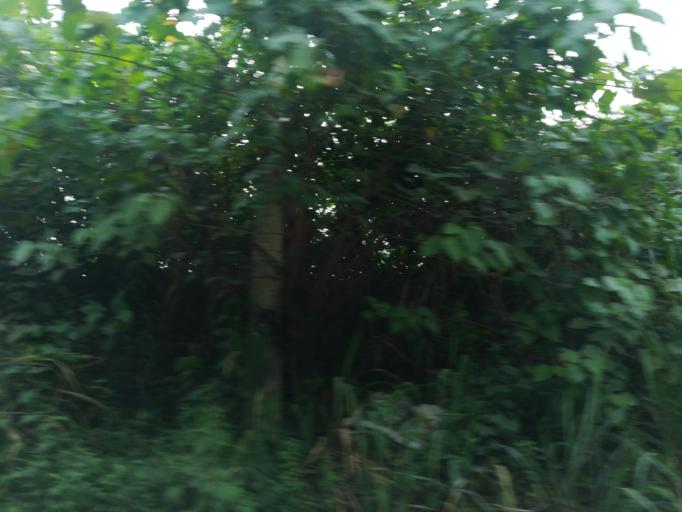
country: NG
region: Lagos
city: Ikeja
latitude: 6.6289
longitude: 3.3642
